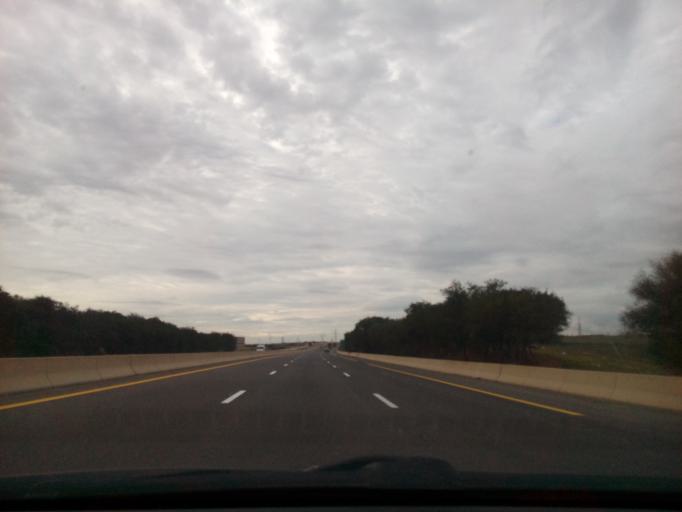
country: DZ
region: Mascara
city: Sig
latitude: 35.5420
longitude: -0.3621
